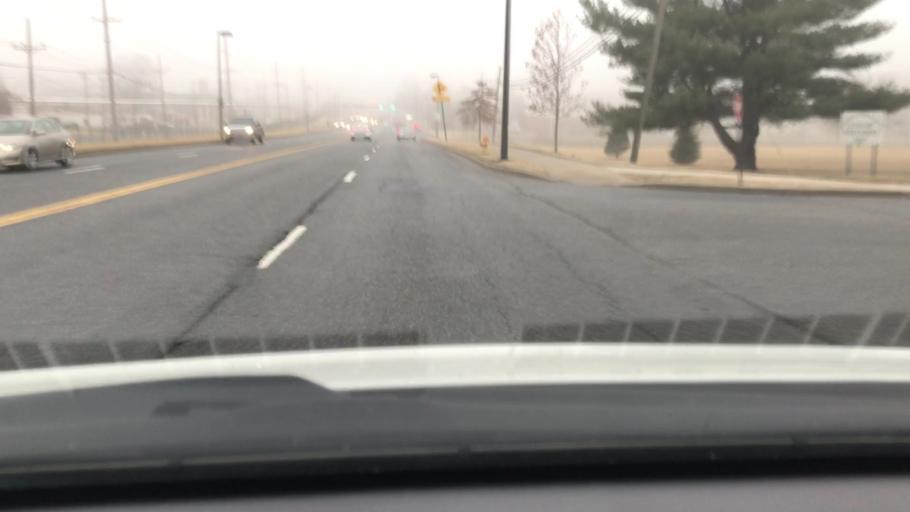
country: US
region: Maryland
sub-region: Frederick County
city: Clover Hill
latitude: 39.4344
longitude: -77.4359
